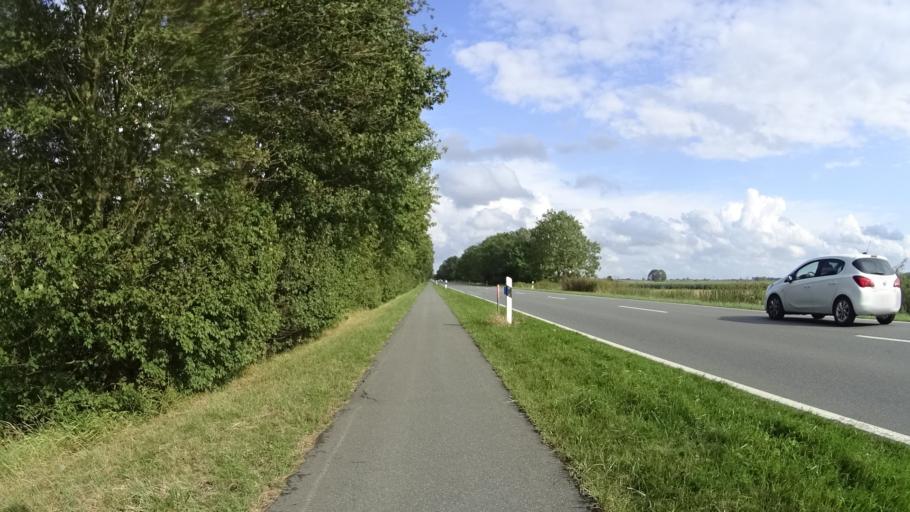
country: DE
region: Lower Saxony
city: Varel
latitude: 53.3927
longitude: 8.1823
